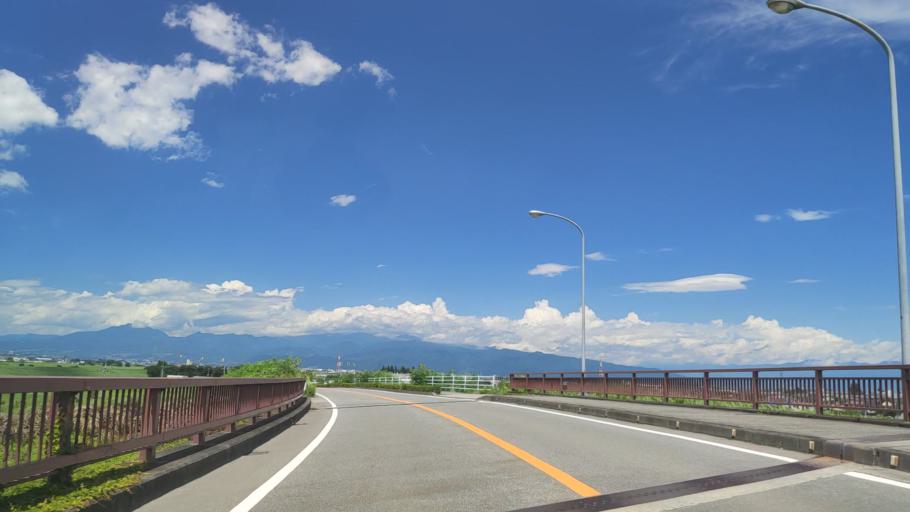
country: JP
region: Yamanashi
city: Ryuo
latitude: 35.5563
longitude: 138.4822
